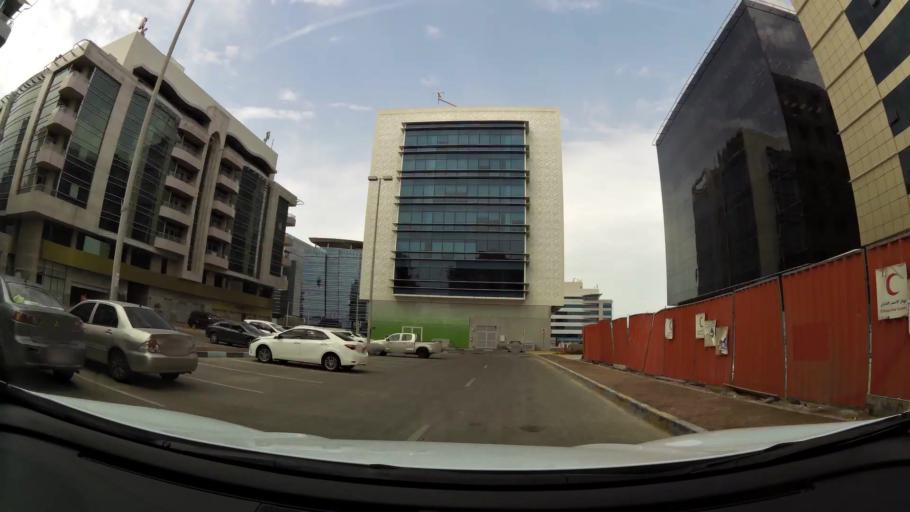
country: AE
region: Abu Dhabi
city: Abu Dhabi
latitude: 24.4307
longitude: 54.4663
